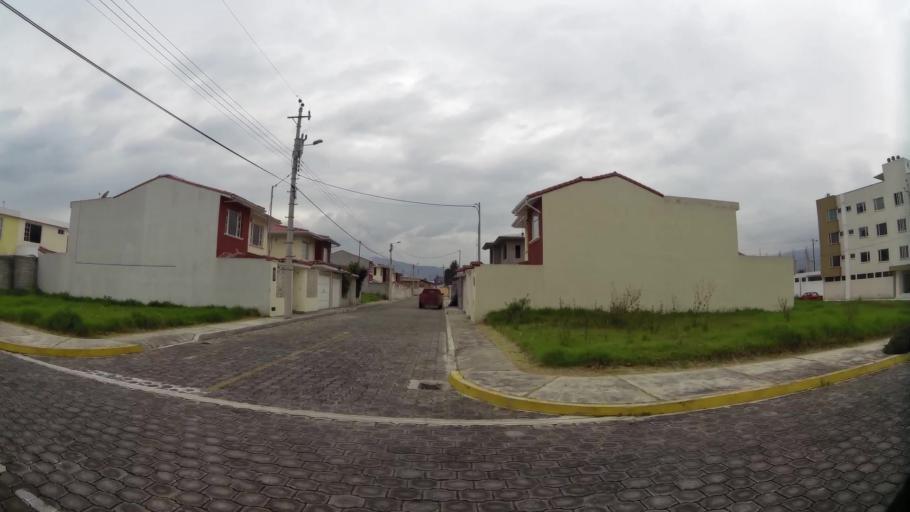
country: EC
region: Pichincha
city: Sangolqui
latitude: -0.3336
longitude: -78.4653
